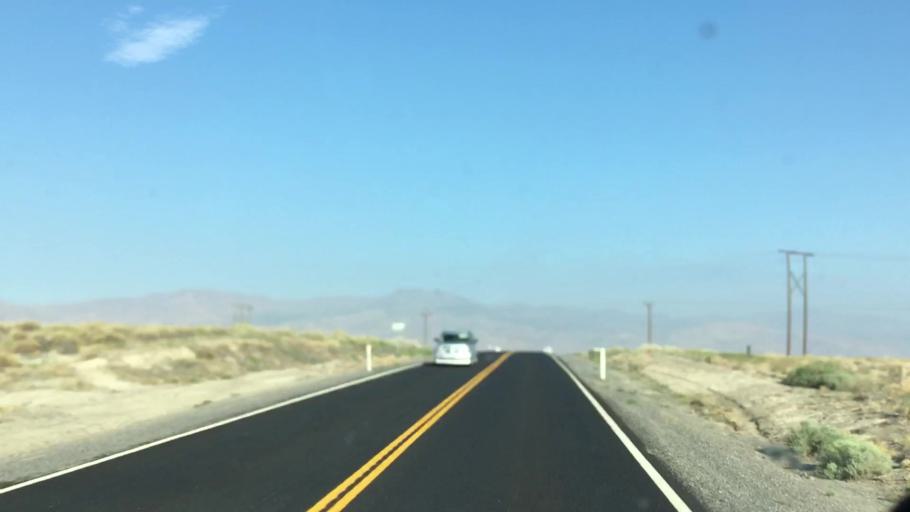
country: US
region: Nevada
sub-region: Lyon County
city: Fernley
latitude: 39.6405
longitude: -119.2975
